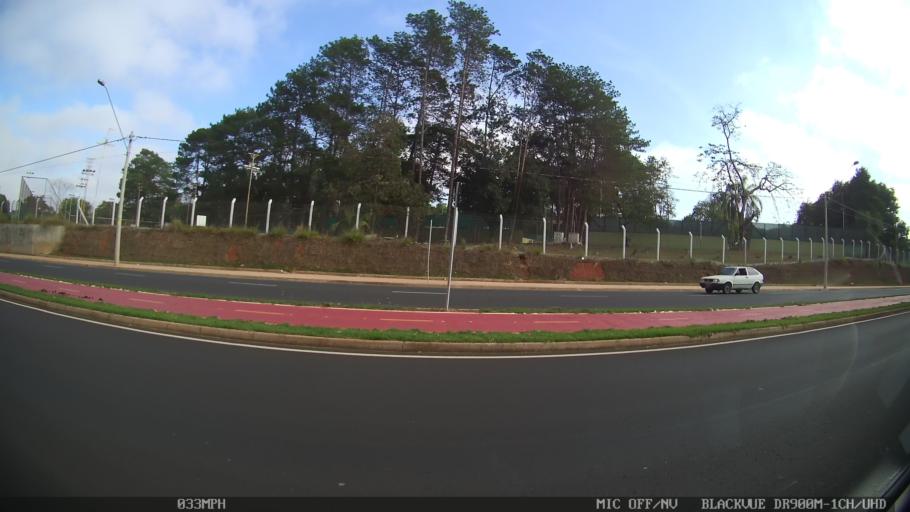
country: BR
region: Sao Paulo
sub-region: Sao Jose Do Rio Preto
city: Sao Jose do Rio Preto
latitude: -20.8106
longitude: -49.4320
